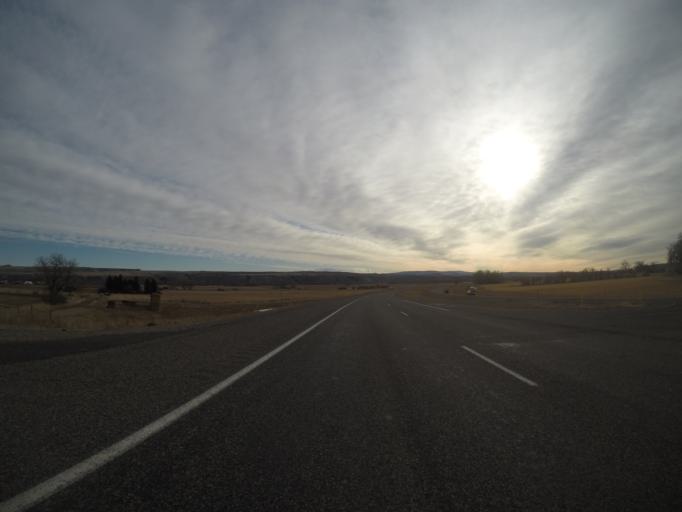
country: US
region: Montana
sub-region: Yellowstone County
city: Laurel
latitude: 45.5412
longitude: -108.8549
